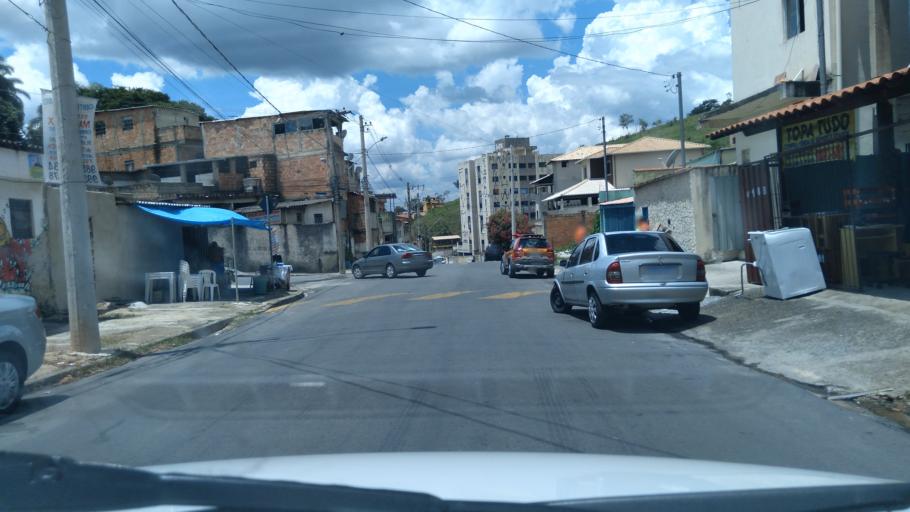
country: BR
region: Minas Gerais
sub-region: Belo Horizonte
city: Belo Horizonte
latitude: -19.8839
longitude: -43.8943
